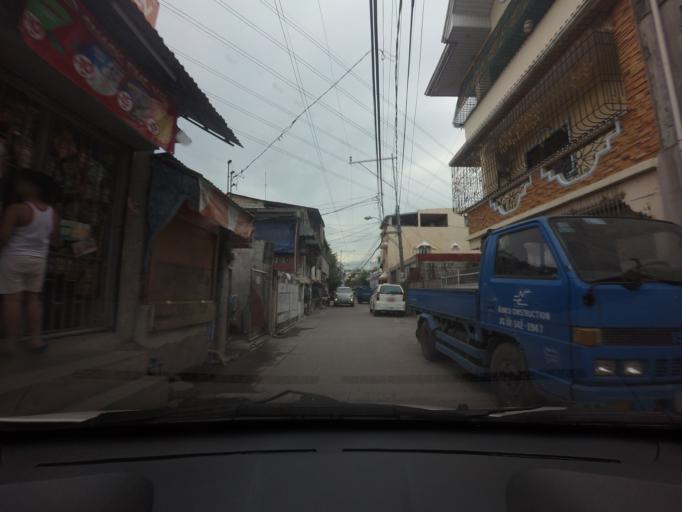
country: PH
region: Calabarzon
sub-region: Province of Rizal
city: Taguig
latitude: 14.5024
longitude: 121.0598
